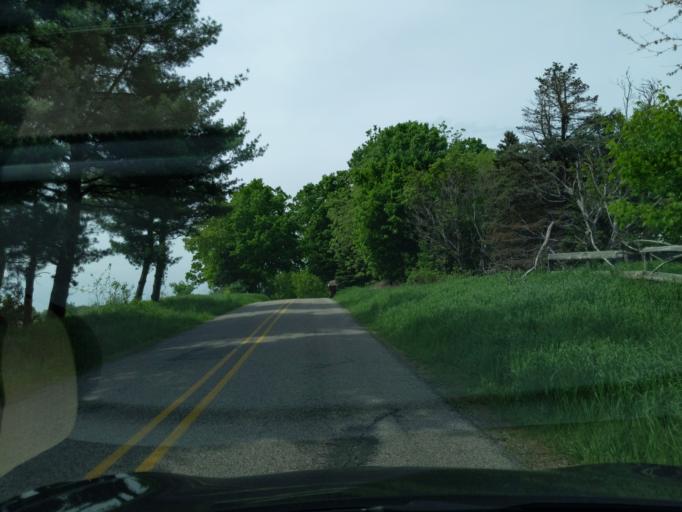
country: US
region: Michigan
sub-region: Ingham County
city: Leslie
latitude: 42.4295
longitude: -84.3361
